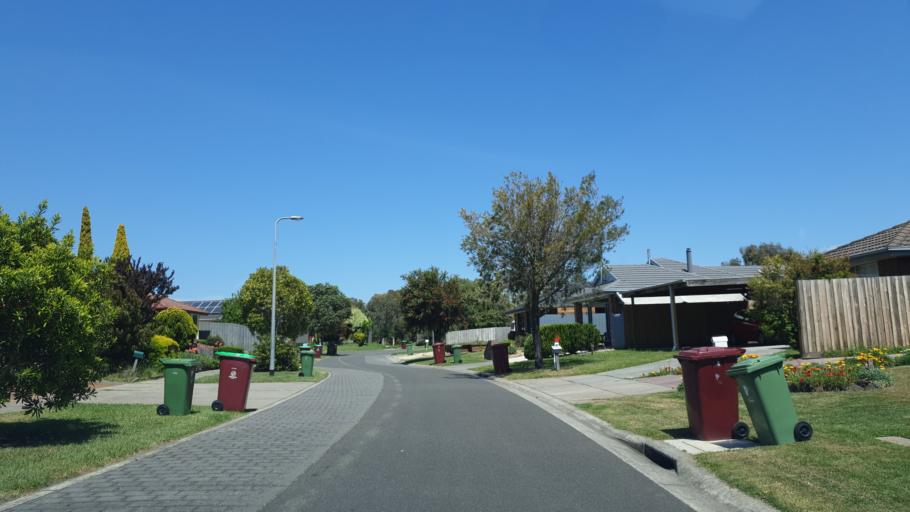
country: AU
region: Victoria
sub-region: Casey
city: Narre Warren South
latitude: -38.0612
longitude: 145.2990
